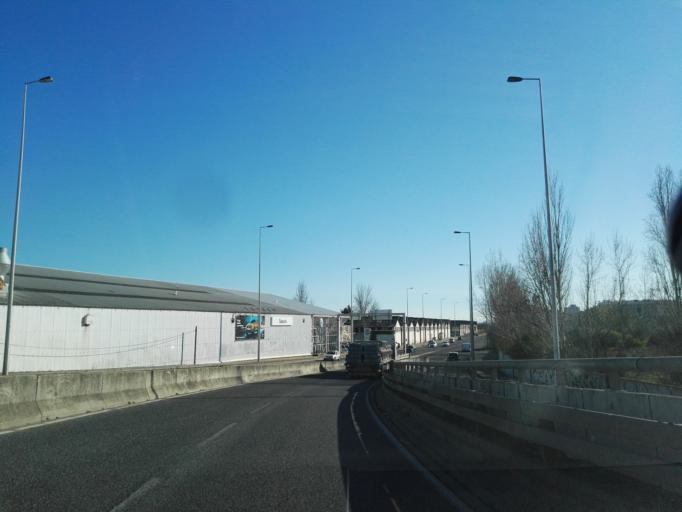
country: PT
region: Lisbon
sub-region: Loures
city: Moscavide
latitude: 38.7531
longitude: -9.0958
